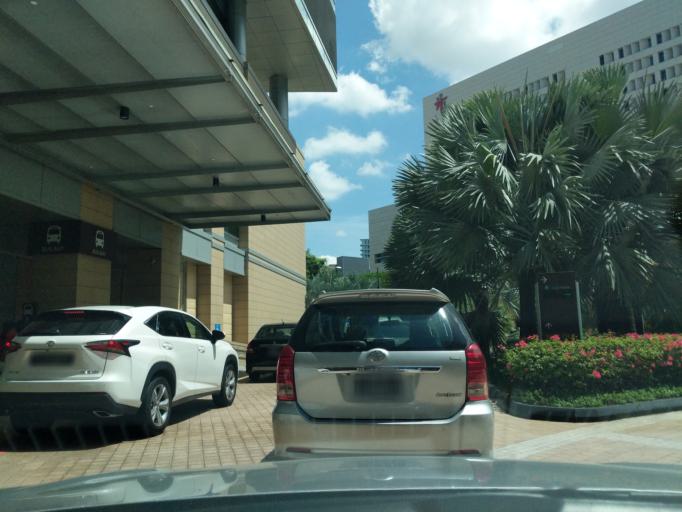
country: SG
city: Singapore
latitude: 1.3216
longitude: 103.8453
